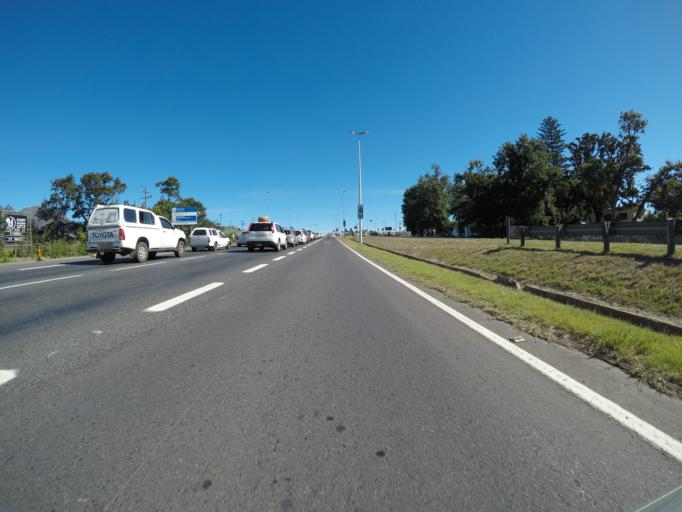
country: ZA
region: Western Cape
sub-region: Cape Winelands District Municipality
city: Stellenbosch
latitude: -33.9957
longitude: 18.8266
